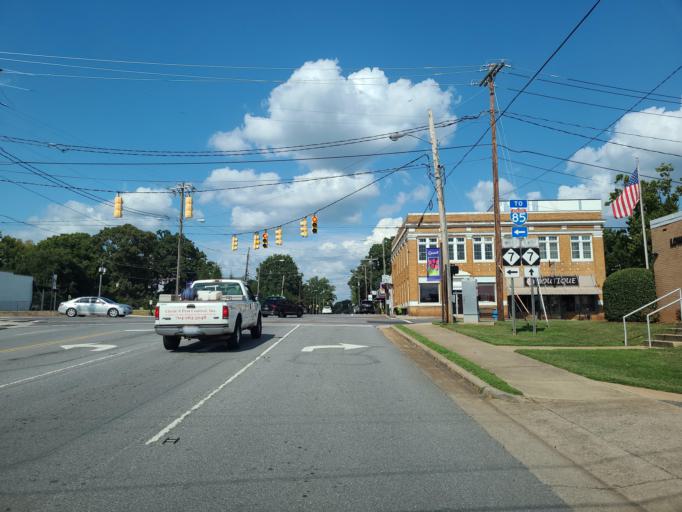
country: US
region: North Carolina
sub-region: Gaston County
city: Lowell
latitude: 35.2664
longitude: -81.1015
